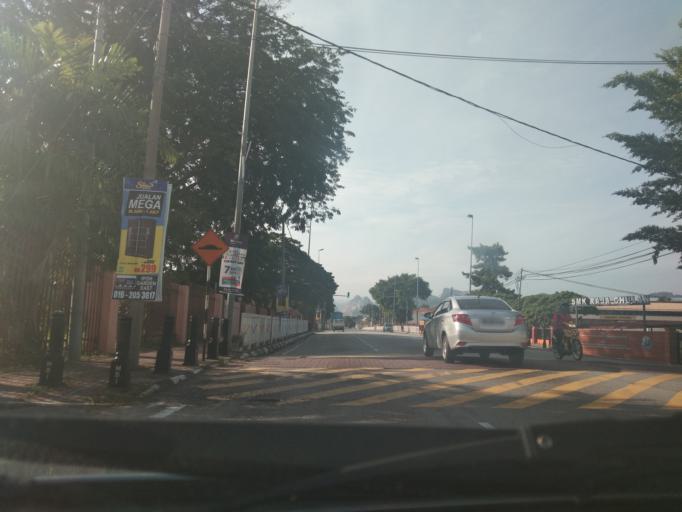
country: MY
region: Perak
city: Ipoh
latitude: 4.5908
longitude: 101.1247
